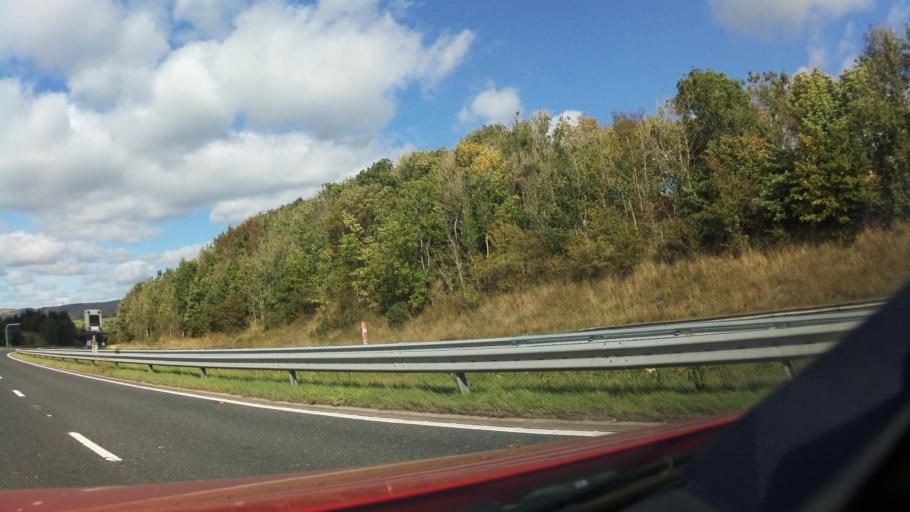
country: GB
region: England
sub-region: Cumbria
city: Sedbergh
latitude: 54.3485
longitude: -2.6165
